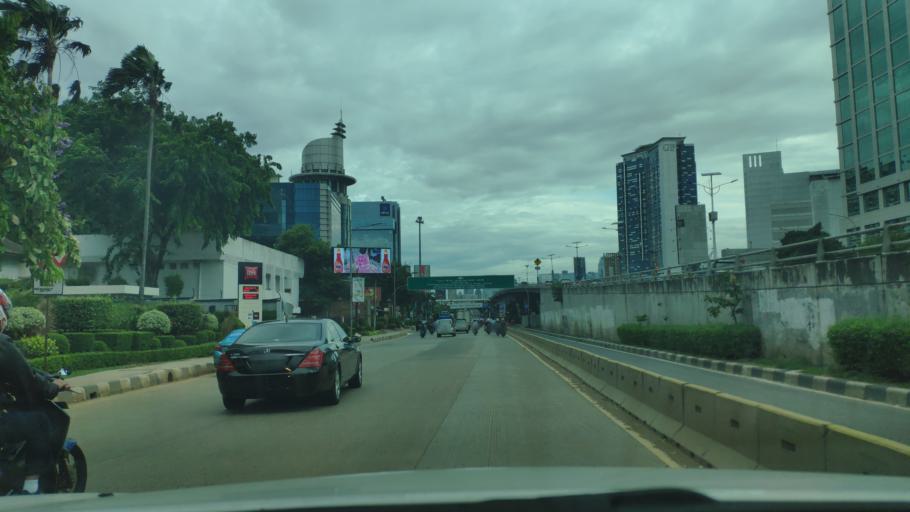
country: ID
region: Jakarta Raya
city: Jakarta
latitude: -6.1994
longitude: 106.7988
